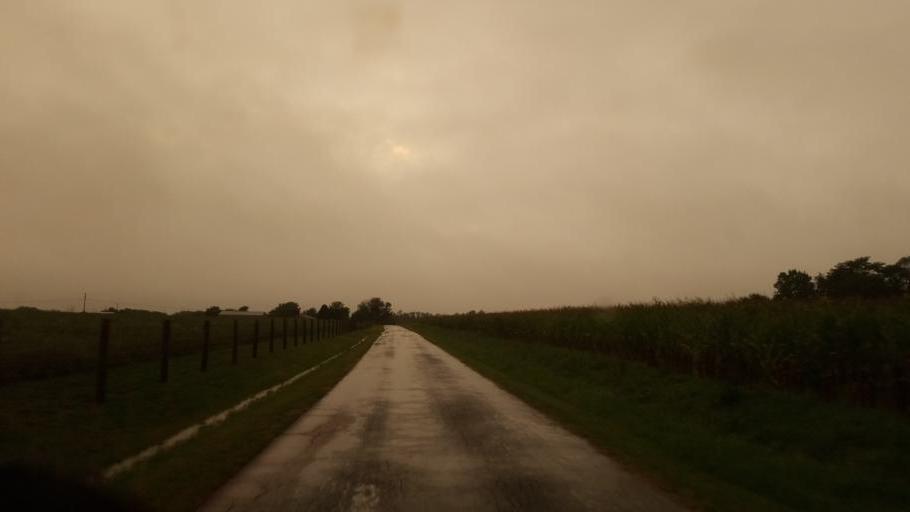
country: US
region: Kentucky
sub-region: Fleming County
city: Flemingsburg
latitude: 38.4680
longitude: -83.6313
